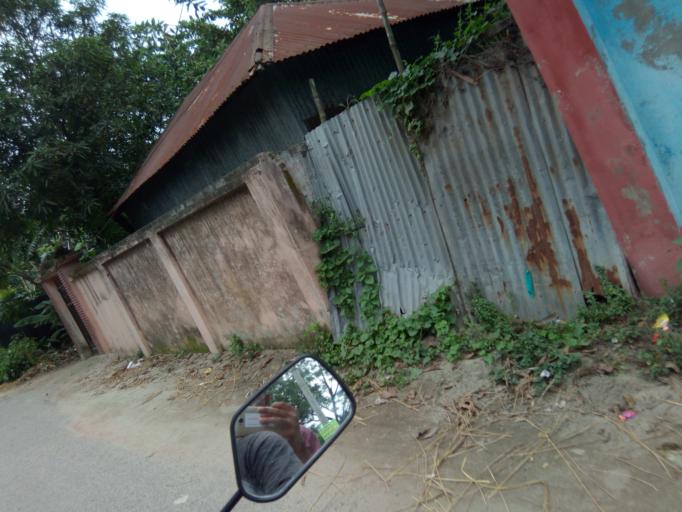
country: BD
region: Dhaka
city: Paltan
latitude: 23.7475
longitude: 90.4861
